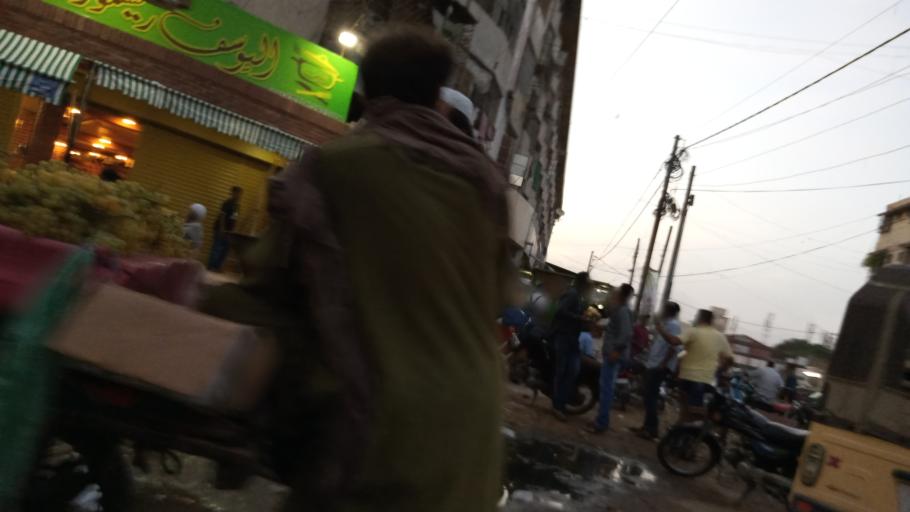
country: PK
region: Sindh
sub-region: Karachi District
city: Karachi
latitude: 24.9395
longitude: 67.0814
